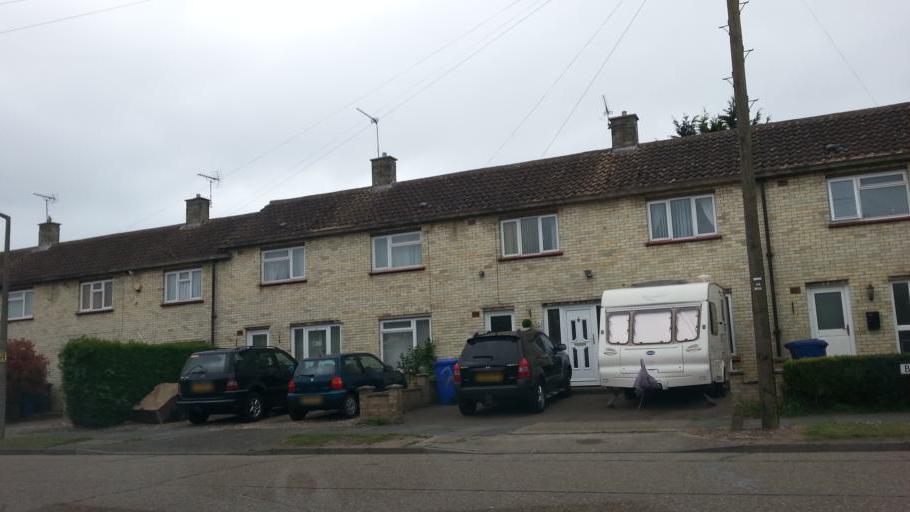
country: GB
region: England
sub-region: Suffolk
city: Bury St Edmunds
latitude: 52.2620
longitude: 0.6992
